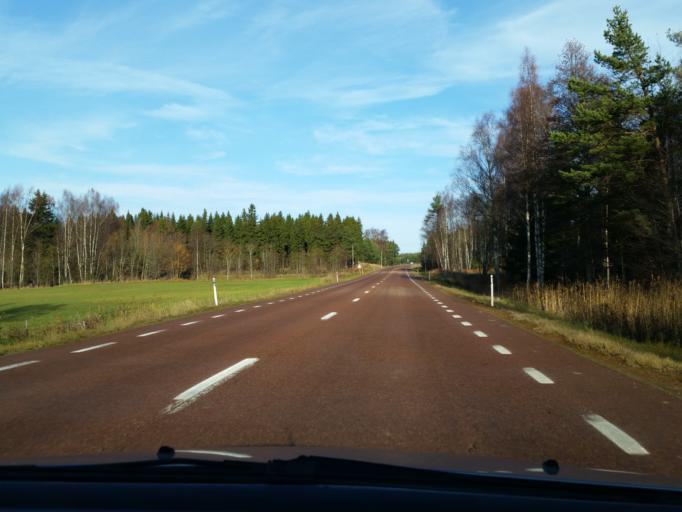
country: AX
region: Alands landsbygd
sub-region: Finstroem
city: Finstroem
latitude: 60.2980
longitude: 19.9528
